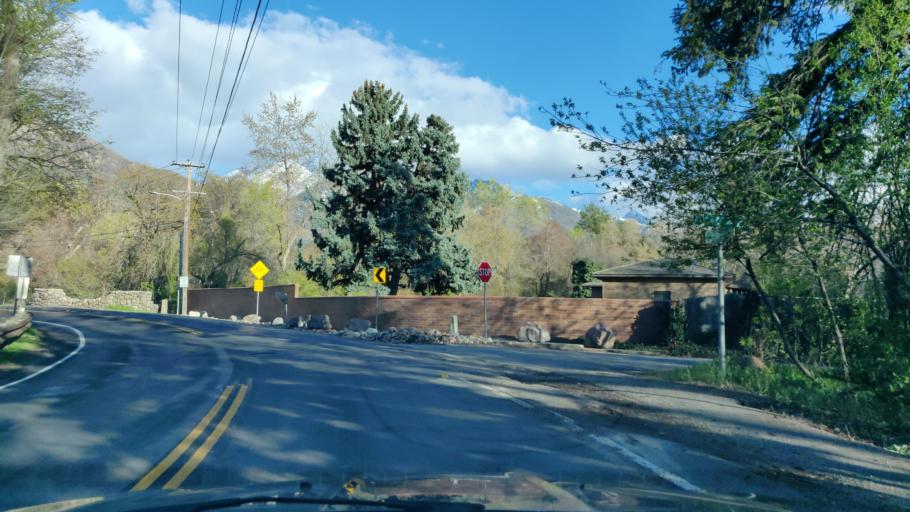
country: US
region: Utah
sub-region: Salt Lake County
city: Cottonwood Heights
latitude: 40.6379
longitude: -111.8137
